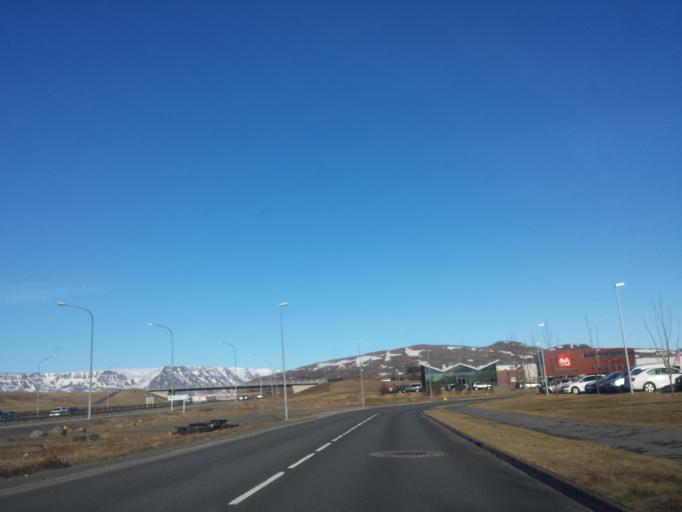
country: IS
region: Capital Region
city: Mosfellsbaer
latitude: 64.1305
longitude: -21.7665
